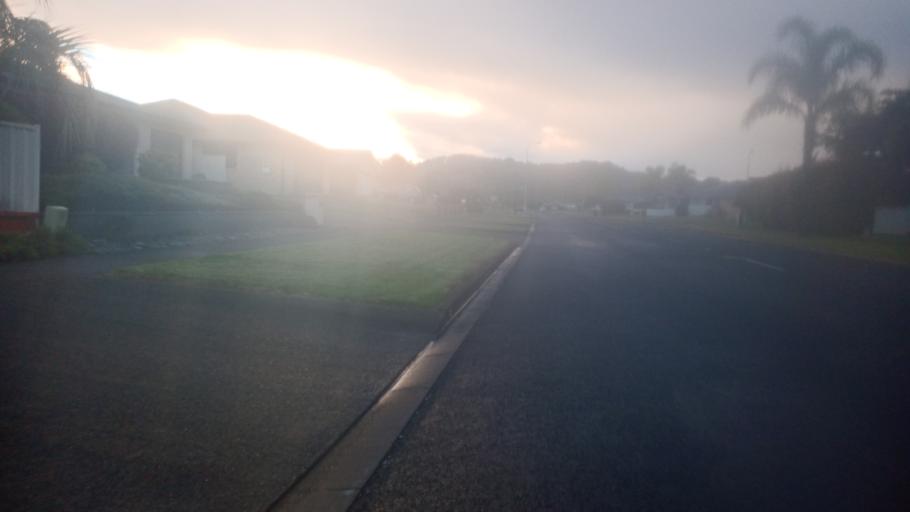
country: NZ
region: Gisborne
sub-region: Gisborne District
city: Gisborne
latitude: -38.6408
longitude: 177.9948
